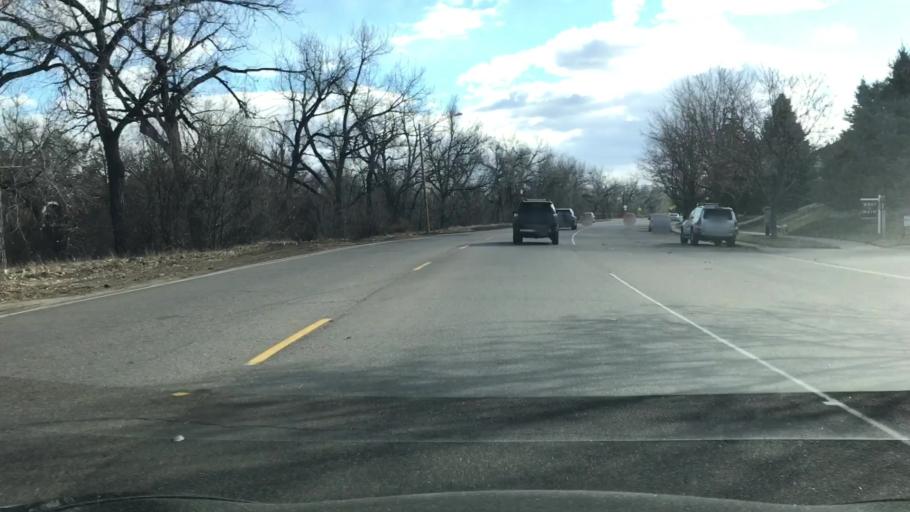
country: US
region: Colorado
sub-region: Arapahoe County
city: Glendale
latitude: 39.7020
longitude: -104.9288
